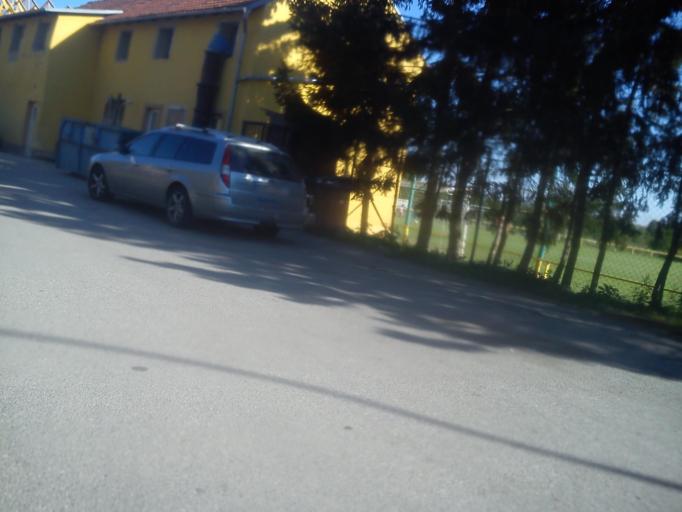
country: CZ
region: South Moravian
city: Sokolnice
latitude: 49.1035
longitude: 16.7576
